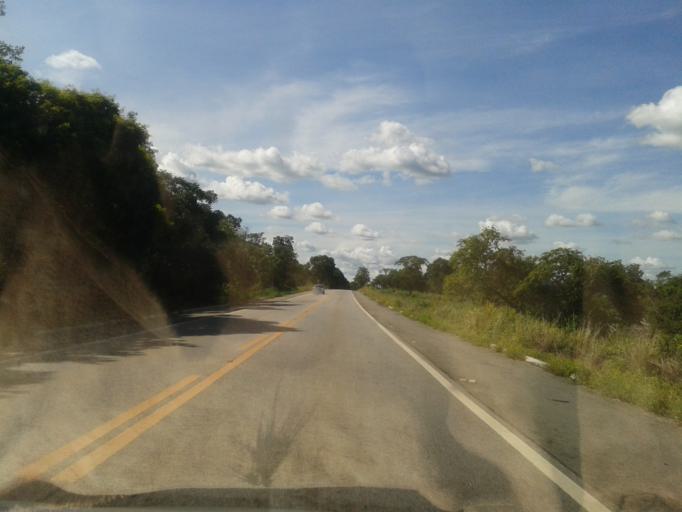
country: BR
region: Goias
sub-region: Mozarlandia
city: Mozarlandia
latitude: -15.2191
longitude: -50.5296
